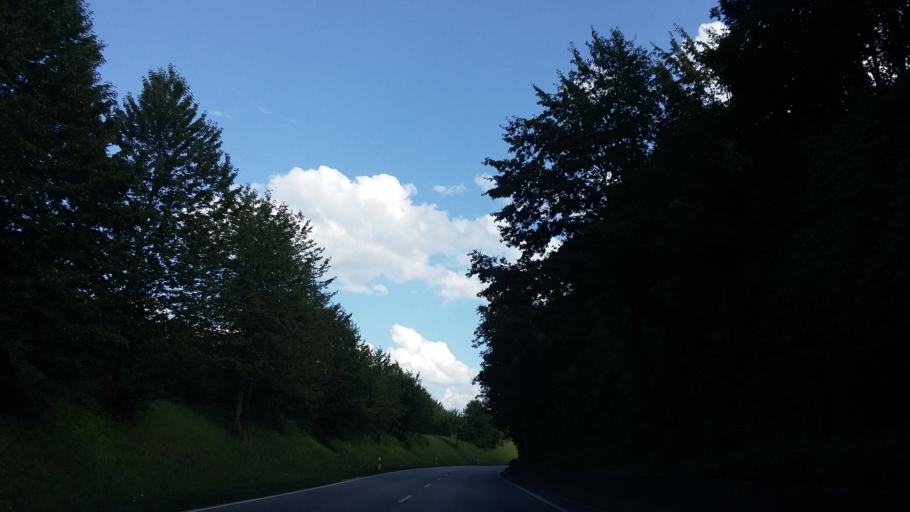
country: DE
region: Bavaria
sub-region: Swabia
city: Guenzburg
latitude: 48.4565
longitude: 10.2879
